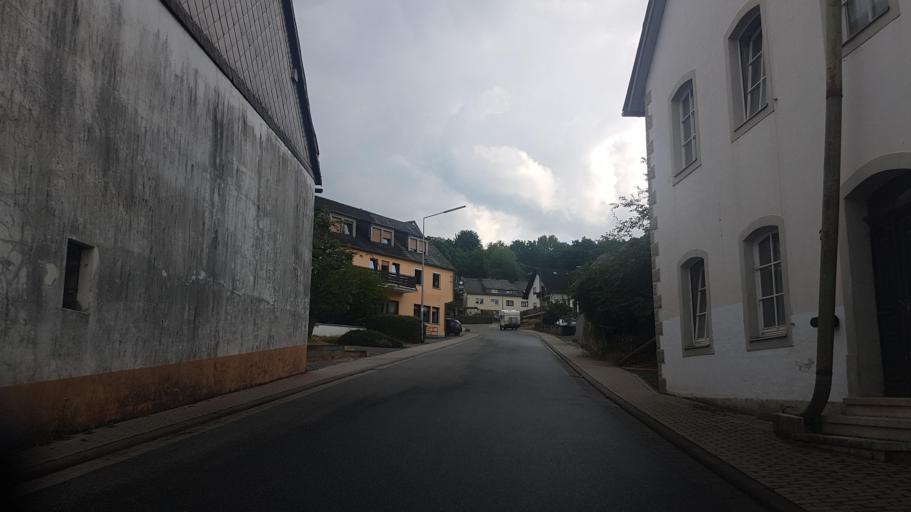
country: DE
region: Rheinland-Pfalz
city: Deuselbach
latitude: 49.7514
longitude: 7.0558
